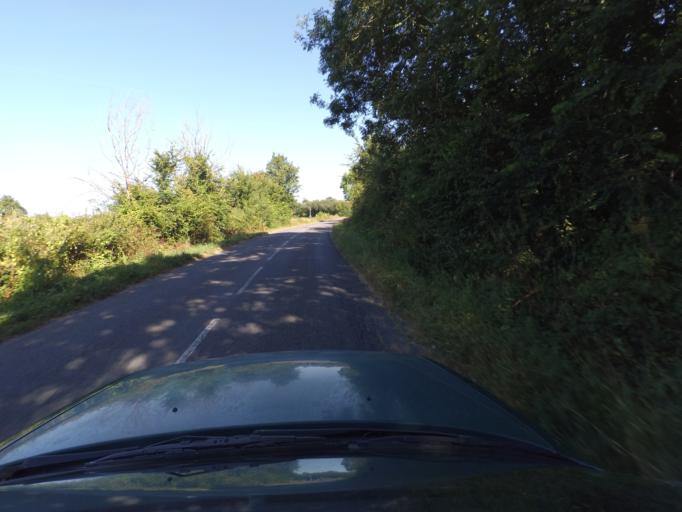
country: FR
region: Pays de la Loire
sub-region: Departement de la Loire-Atlantique
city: Maisdon-sur-Sevre
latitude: 47.1054
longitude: -1.4039
